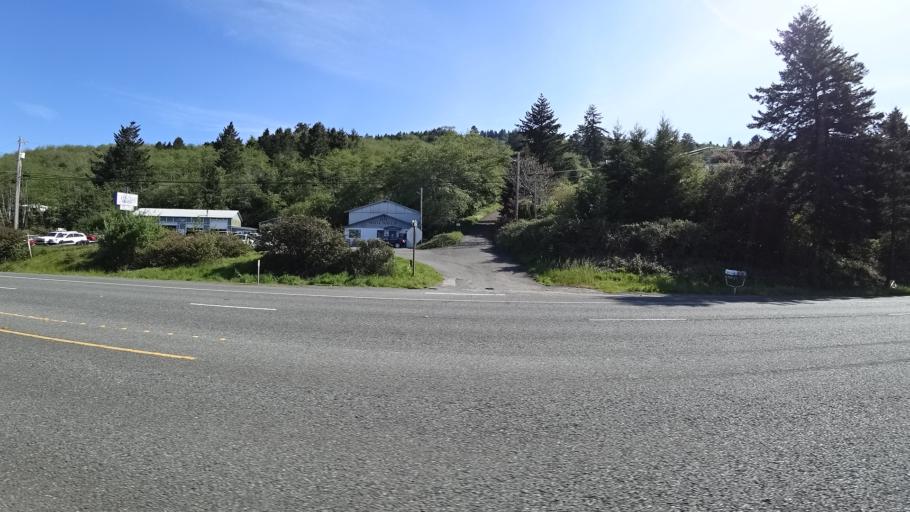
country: US
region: Oregon
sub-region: Curry County
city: Harbor
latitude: 42.0254
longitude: -124.2299
